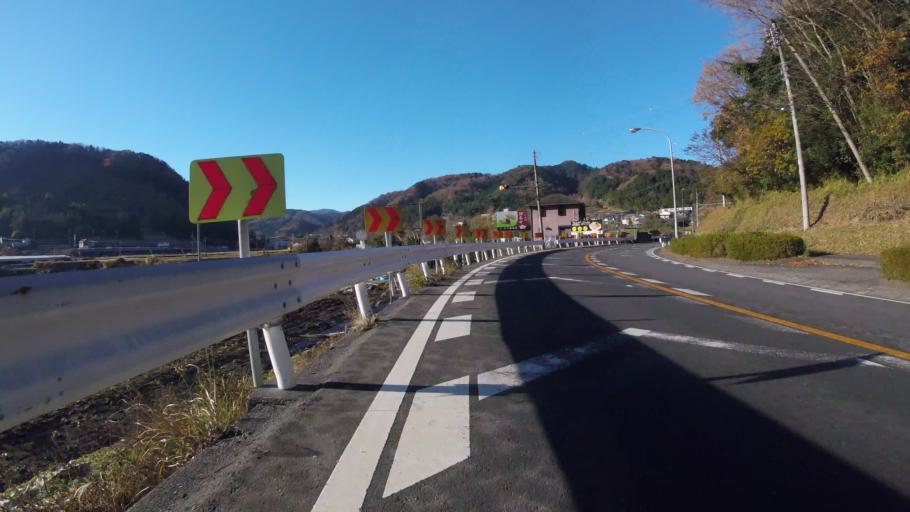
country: JP
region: Shizuoka
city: Heda
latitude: 34.9205
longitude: 138.9287
